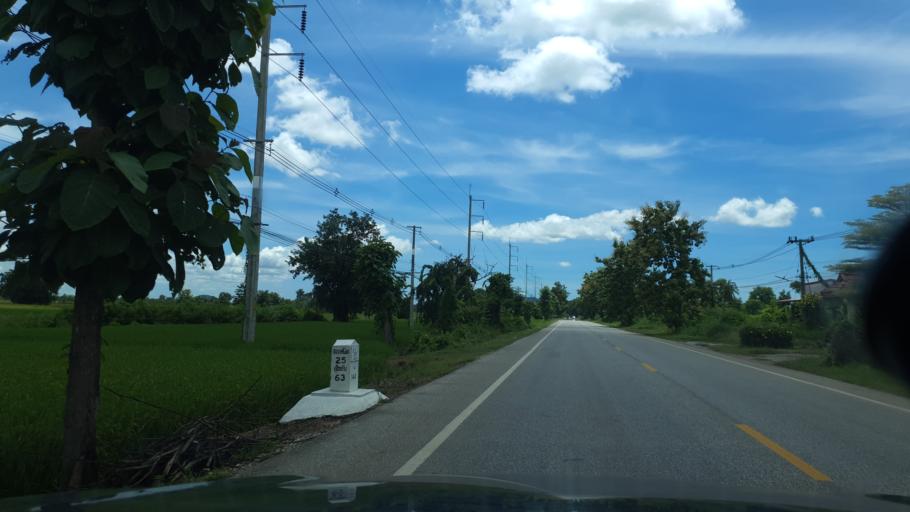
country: TH
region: Sukhothai
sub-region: Amphoe Si Satchanalai
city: Si Satchanalai
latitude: 17.4868
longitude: 99.7609
